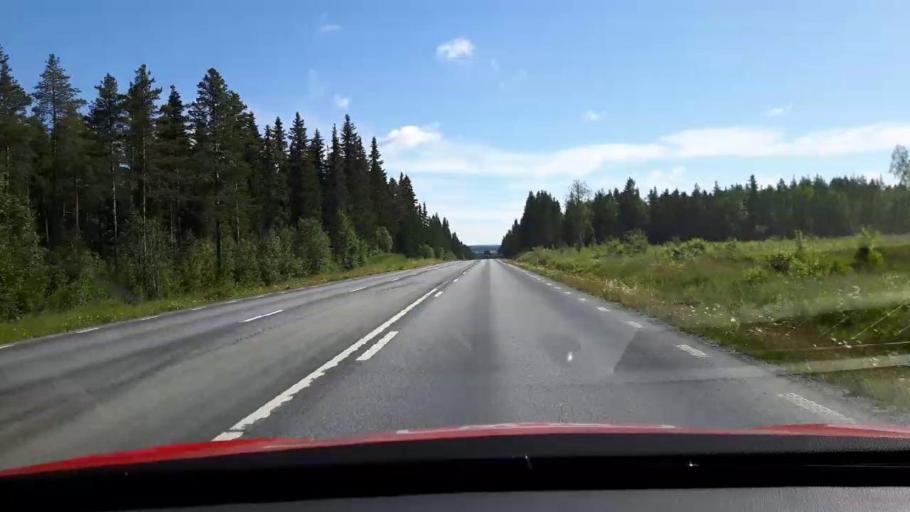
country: SE
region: Jaemtland
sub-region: OEstersunds Kommun
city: Lit
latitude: 63.2489
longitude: 14.7988
